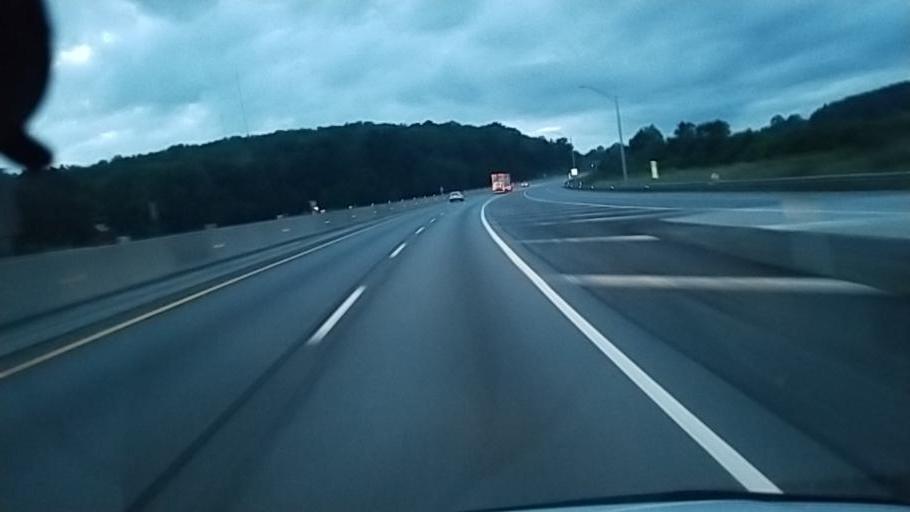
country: US
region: Pennsylvania
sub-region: Somerset County
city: Somerset
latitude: 40.0231
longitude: -79.0870
